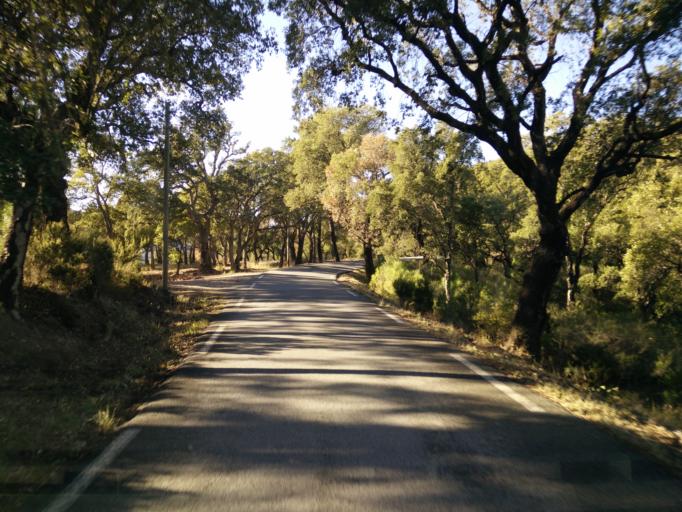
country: FR
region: Provence-Alpes-Cote d'Azur
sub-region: Departement du Var
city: La Garde-Freinet
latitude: 43.2604
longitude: 6.4610
